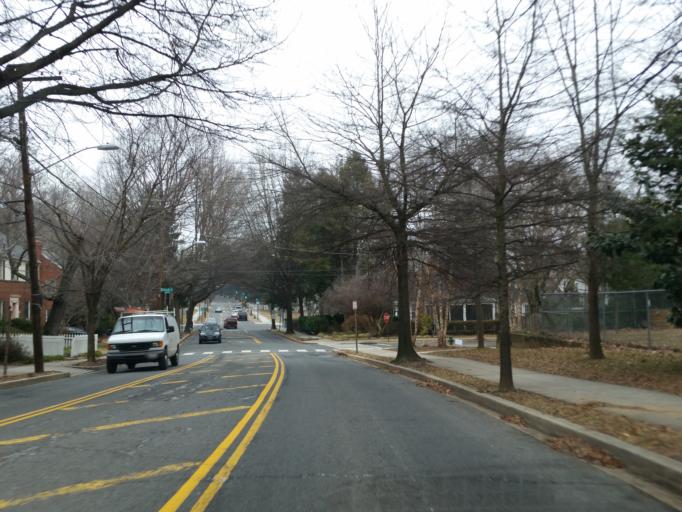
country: US
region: Maryland
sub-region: Montgomery County
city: Chevy Chase Village
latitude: 38.9528
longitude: -77.0716
